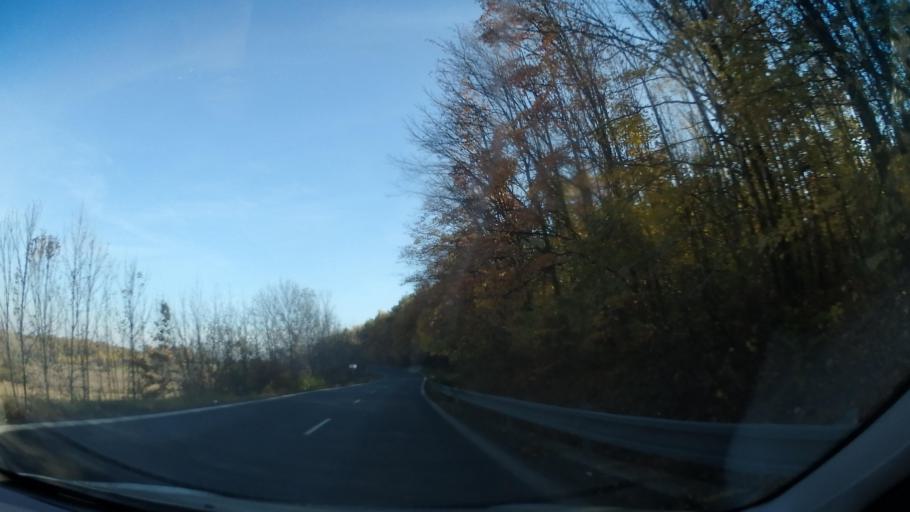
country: CZ
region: Praha
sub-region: Praha 14
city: Dolni Pocernice
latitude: 50.0619
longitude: 14.6024
